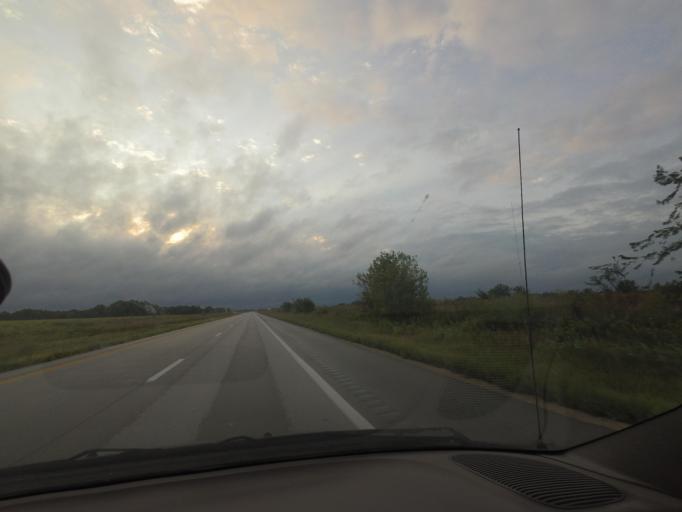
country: US
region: Missouri
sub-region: Shelby County
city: Shelbina
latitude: 39.6801
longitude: -91.9815
